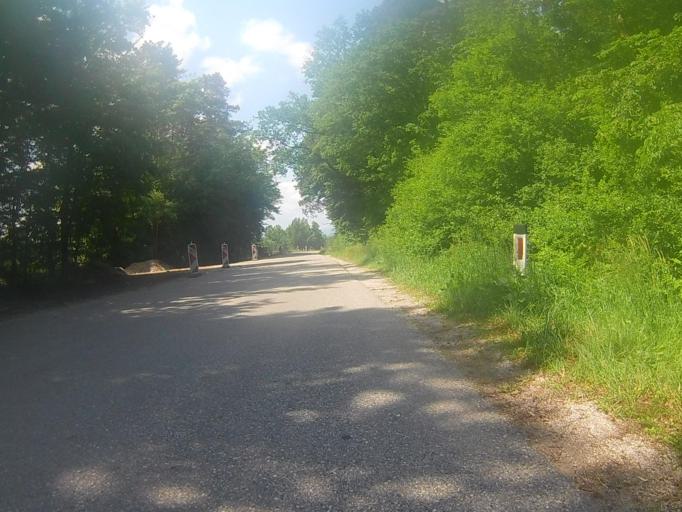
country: SI
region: Kidricevo
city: Kidricevo
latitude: 46.4288
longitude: 15.7637
